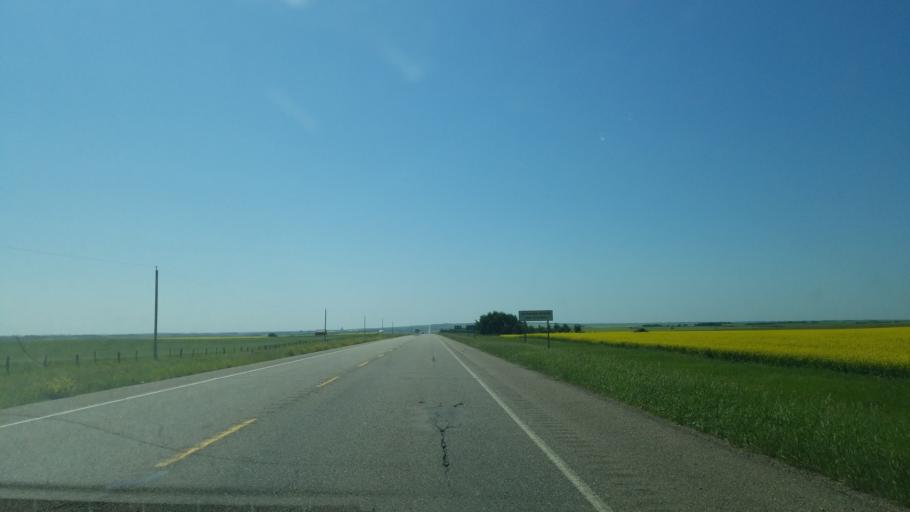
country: CA
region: Saskatchewan
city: Macklin
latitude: 52.3613
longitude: -110.0236
